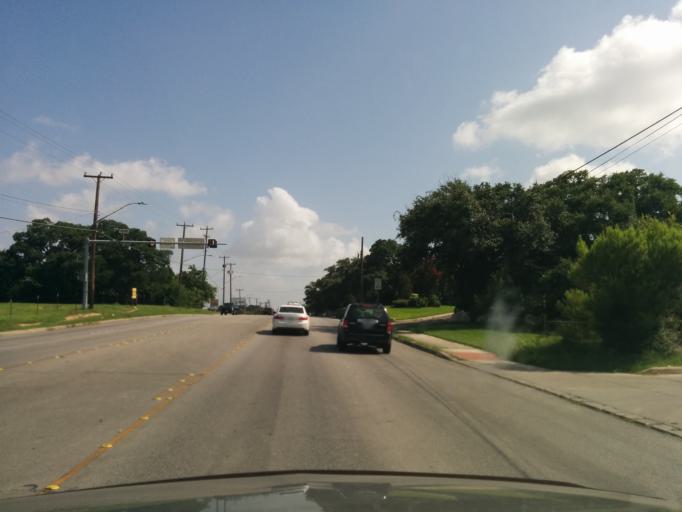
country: US
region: Texas
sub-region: Bexar County
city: Leon Valley
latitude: 29.5528
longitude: -98.6149
